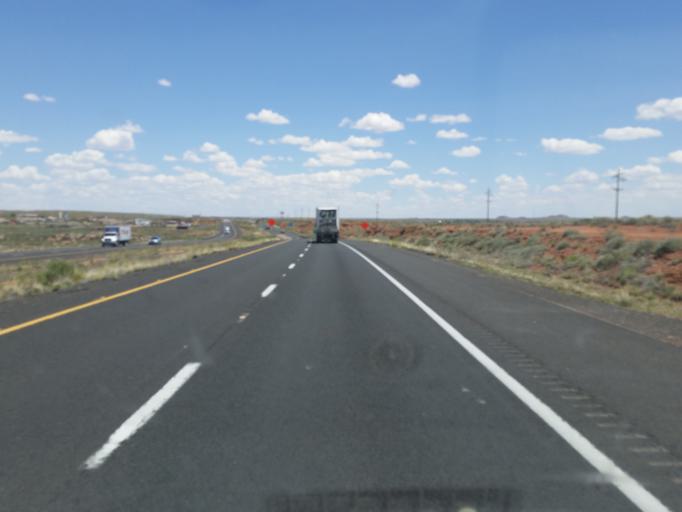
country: US
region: Arizona
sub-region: Navajo County
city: Holbrook
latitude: 34.9105
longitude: -110.2376
